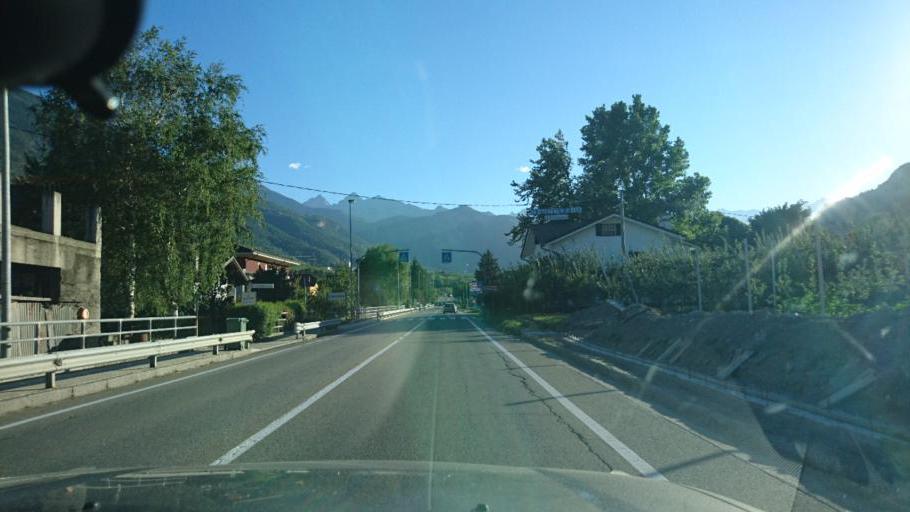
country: IT
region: Aosta Valley
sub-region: Valle d'Aosta
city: Saint Maurice
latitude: 45.7165
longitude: 7.2600
